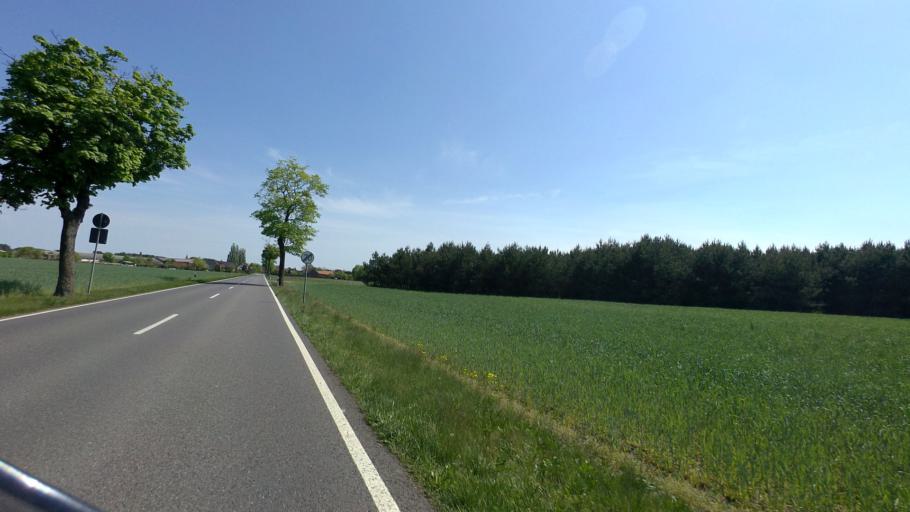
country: DE
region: Brandenburg
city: Schlepzig
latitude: 52.0607
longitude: 13.9479
